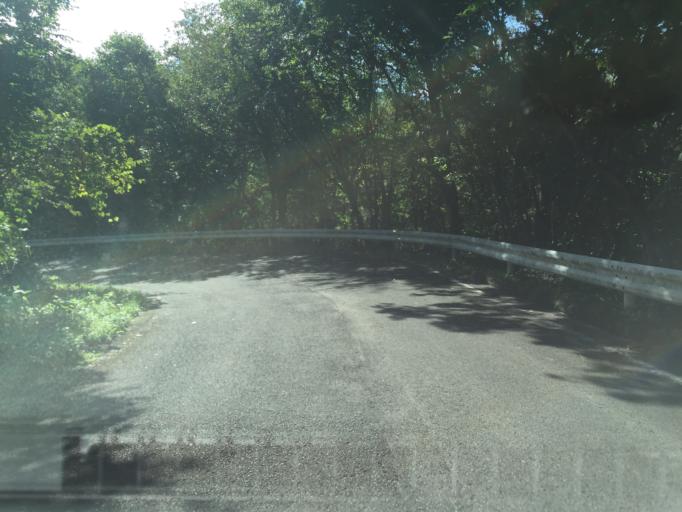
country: JP
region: Fukushima
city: Yanagawamachi-saiwaicho
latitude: 37.8339
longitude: 140.7002
